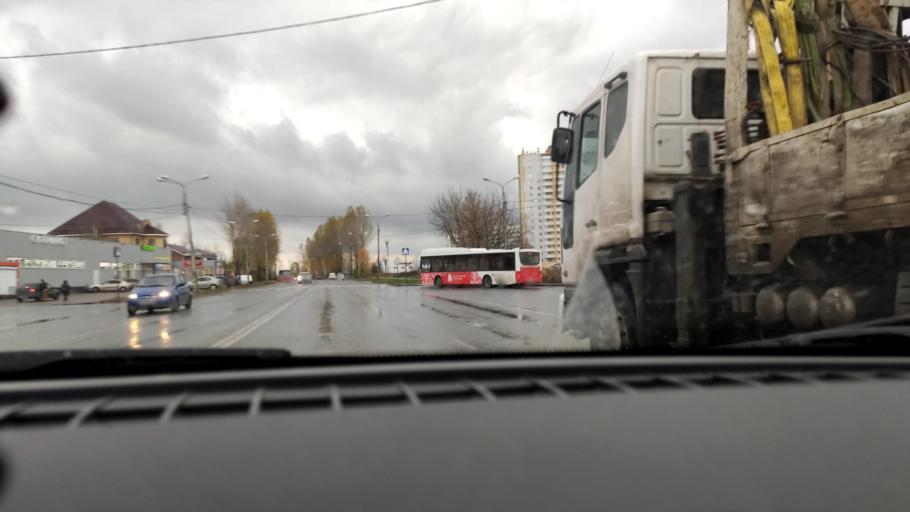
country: RU
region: Perm
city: Perm
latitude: 58.0537
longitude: 56.3558
